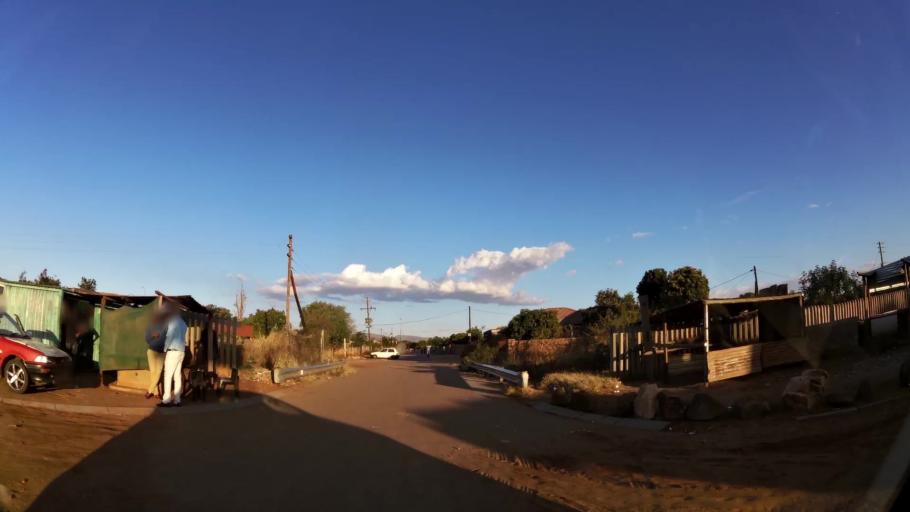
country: ZA
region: Limpopo
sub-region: Waterberg District Municipality
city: Mokopane
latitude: -24.1424
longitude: 28.9936
